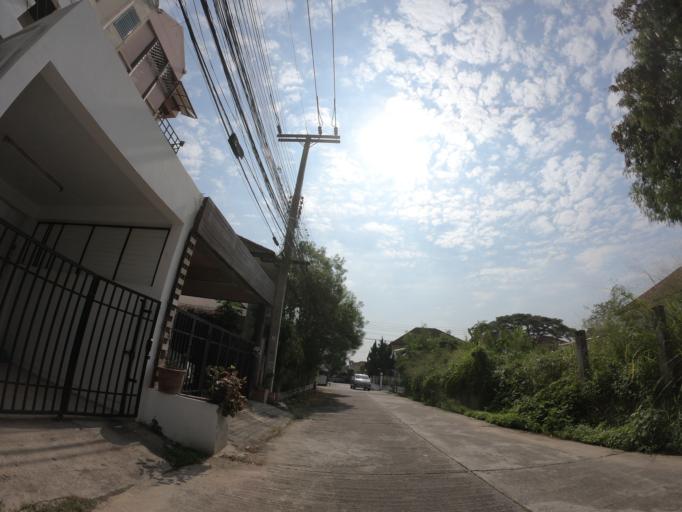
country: TH
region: Chiang Mai
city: Chiang Mai
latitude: 18.7781
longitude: 98.9587
